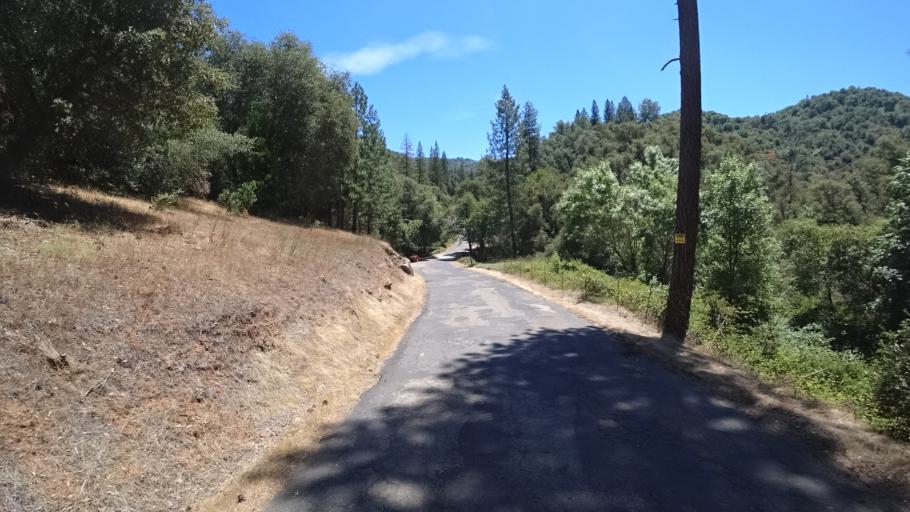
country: US
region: California
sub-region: Calaveras County
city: Forest Meadows
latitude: 38.2032
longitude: -120.4515
